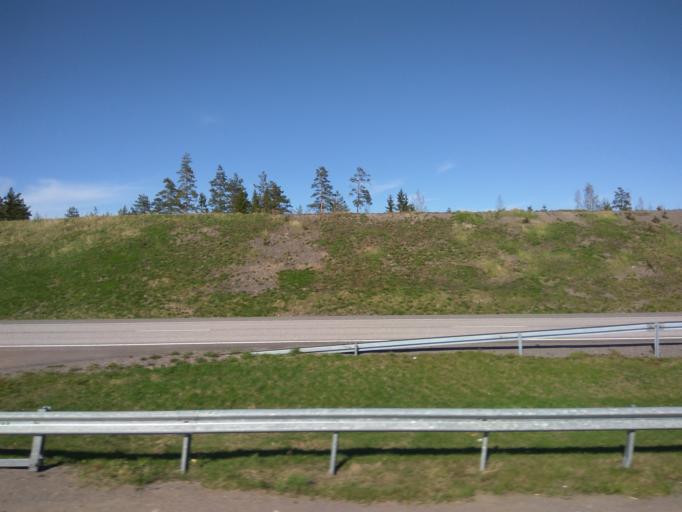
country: FI
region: Uusimaa
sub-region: Loviisa
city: Perna
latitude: 60.4818
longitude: 26.0264
